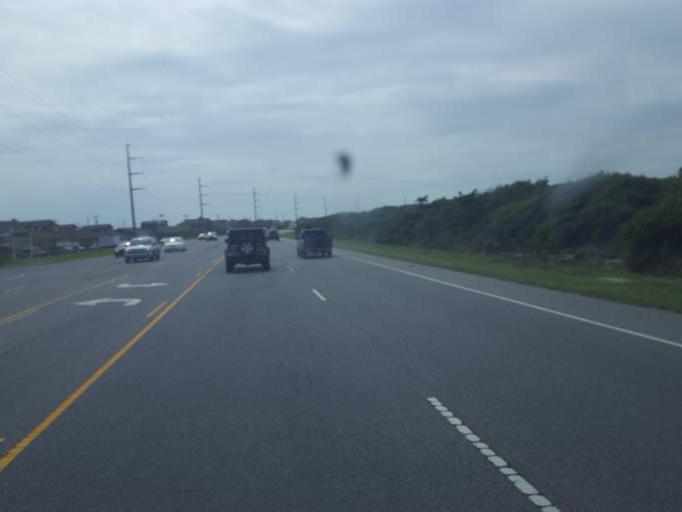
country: US
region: North Carolina
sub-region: Dare County
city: Nags Head
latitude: 35.9649
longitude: -75.6301
